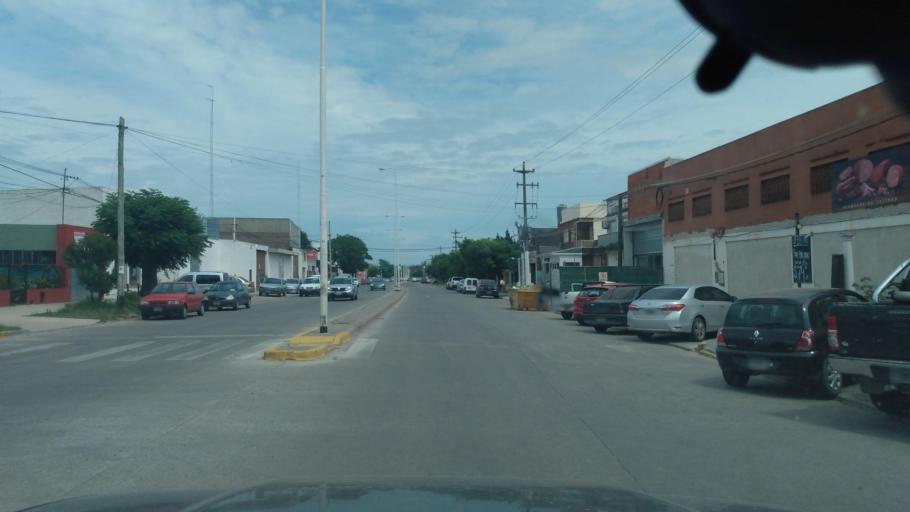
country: AR
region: Buenos Aires
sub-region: Partido de Lujan
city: Lujan
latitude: -34.5649
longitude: -59.0982
